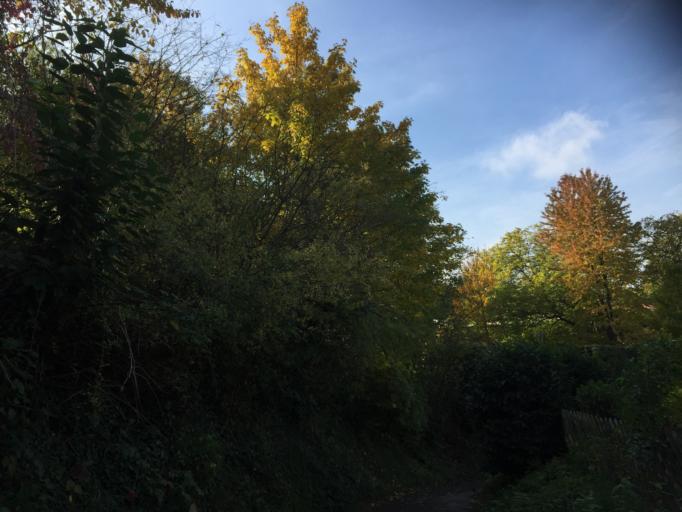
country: DE
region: Hesse
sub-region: Regierungsbezirk Darmstadt
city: Bensheim
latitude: 49.6746
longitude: 8.6406
